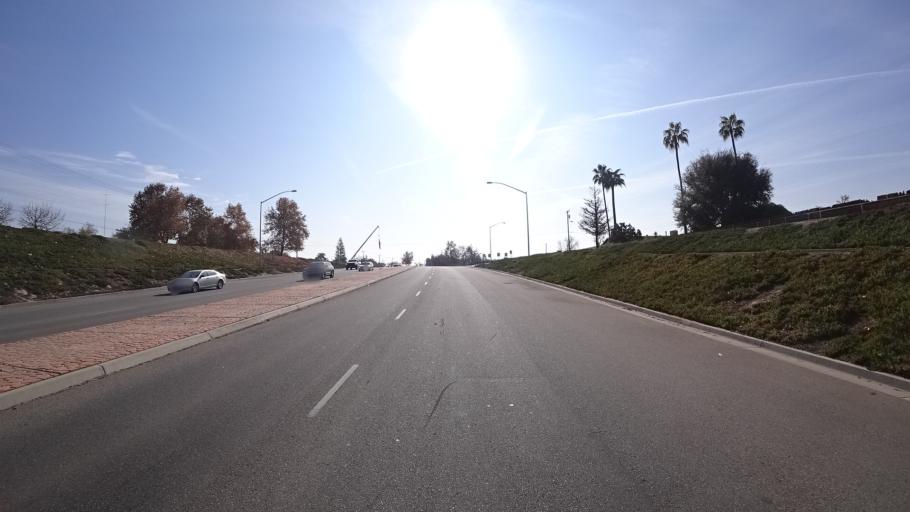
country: US
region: California
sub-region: Kern County
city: Greenacres
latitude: 35.3760
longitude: -119.1105
